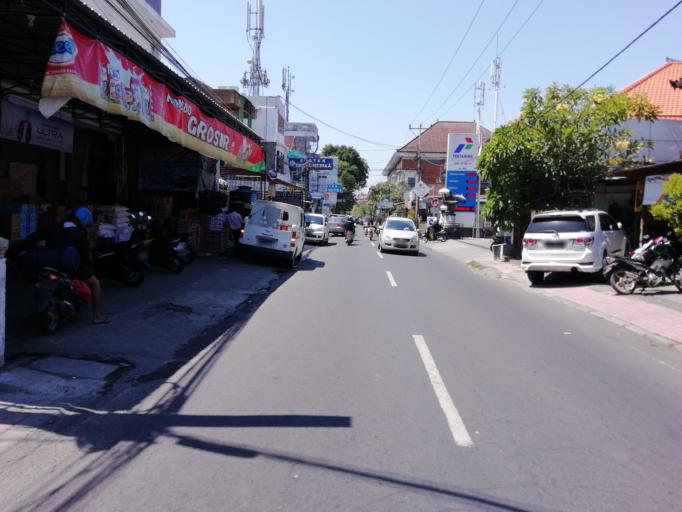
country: ID
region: Bali
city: Karyadharma
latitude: -8.6776
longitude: 115.2114
